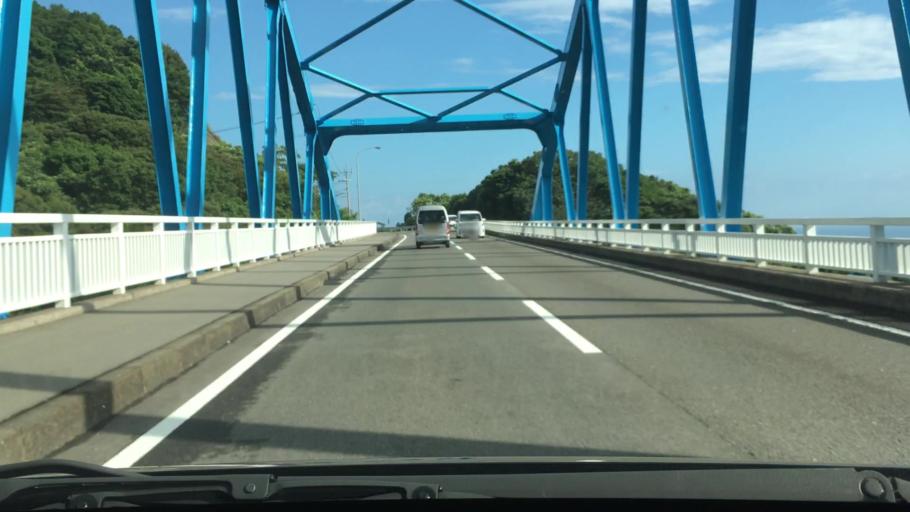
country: JP
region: Nagasaki
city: Togitsu
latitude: 32.8509
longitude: 129.6904
